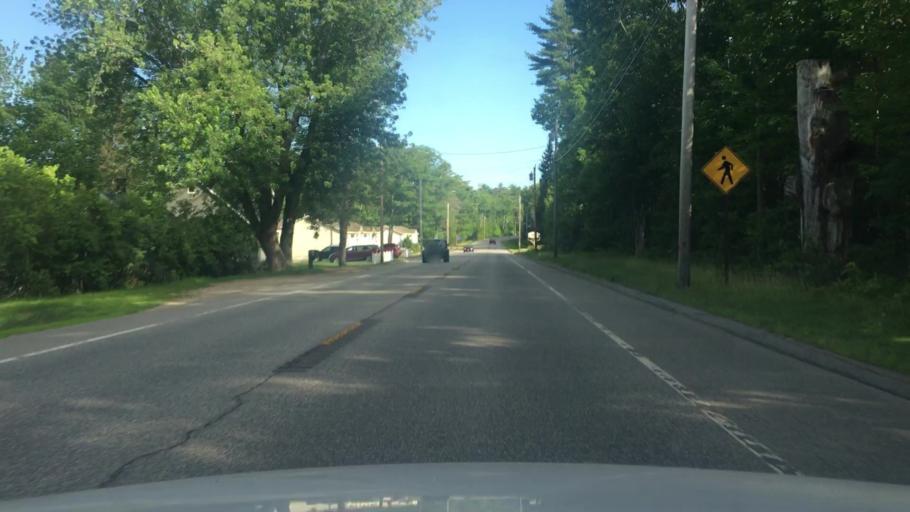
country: US
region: Maine
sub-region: Androscoggin County
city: Livermore Falls
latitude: 44.4378
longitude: -70.2150
